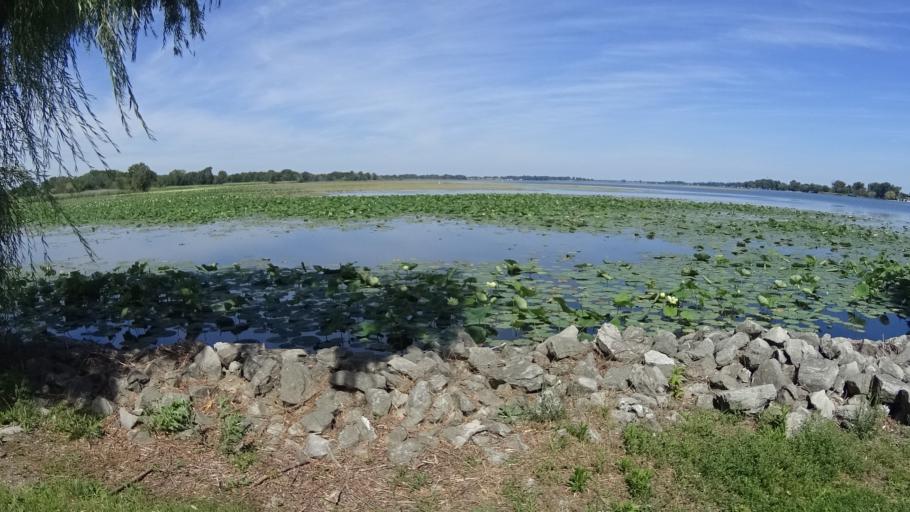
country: US
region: Ohio
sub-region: Erie County
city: Huron
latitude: 41.4291
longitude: -82.6231
